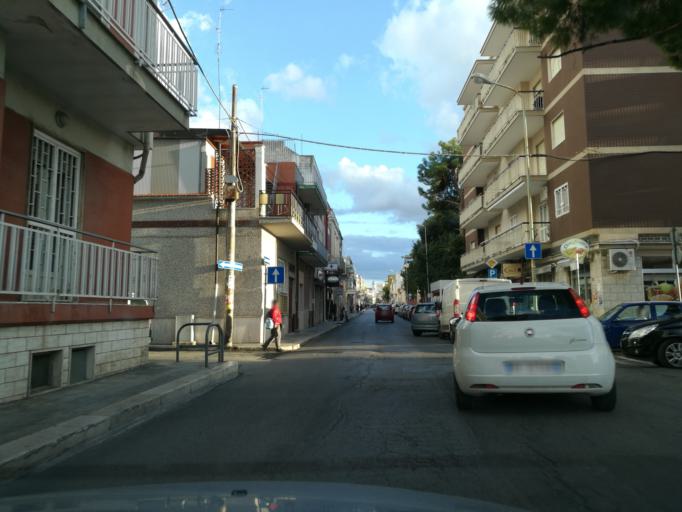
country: IT
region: Apulia
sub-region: Provincia di Bari
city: Valenzano
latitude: 41.0472
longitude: 16.8838
